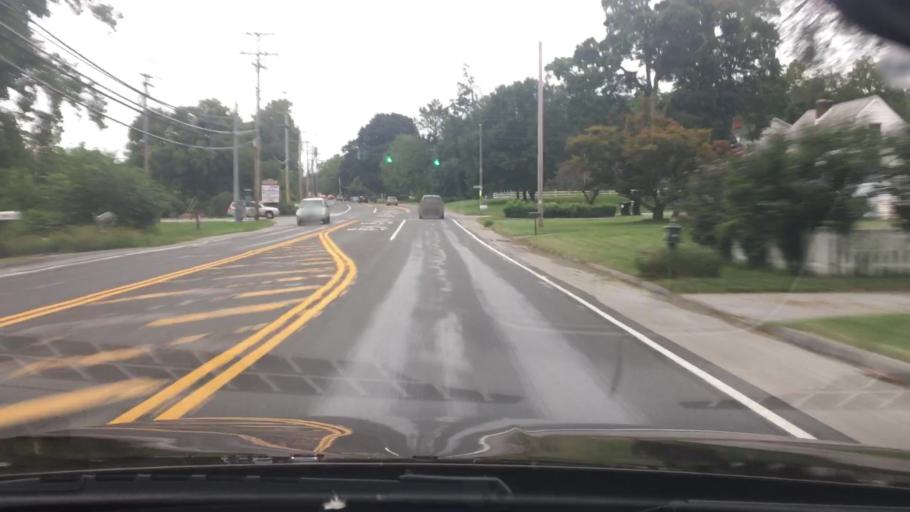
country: US
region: New York
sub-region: Dutchess County
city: Arlington
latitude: 41.7087
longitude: -73.8667
